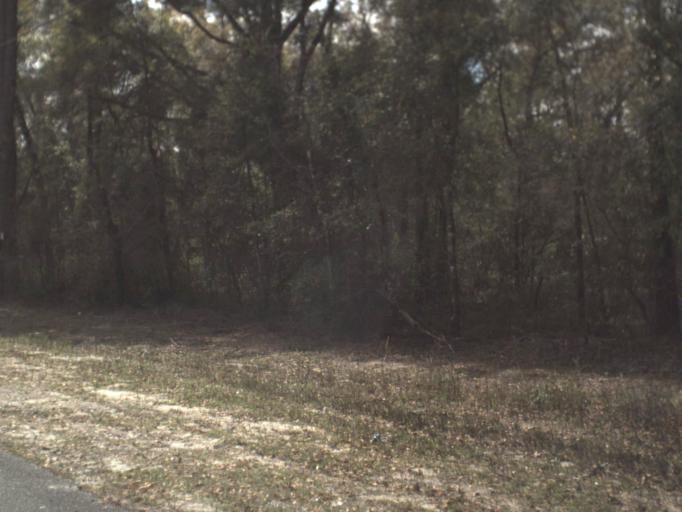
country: US
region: Florida
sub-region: Wakulla County
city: Crawfordville
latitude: 30.1570
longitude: -84.3819
